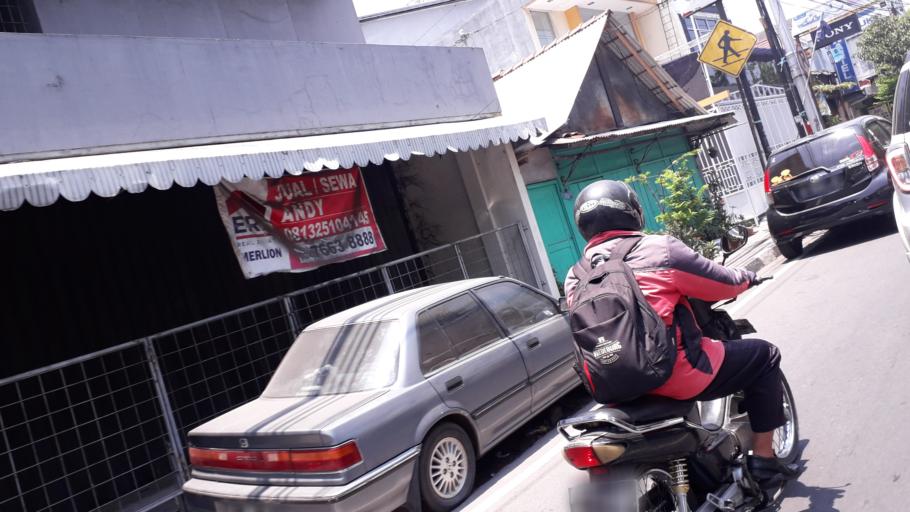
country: ID
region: Daerah Istimewa Yogyakarta
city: Yogyakarta
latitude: -7.7796
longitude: 110.3610
